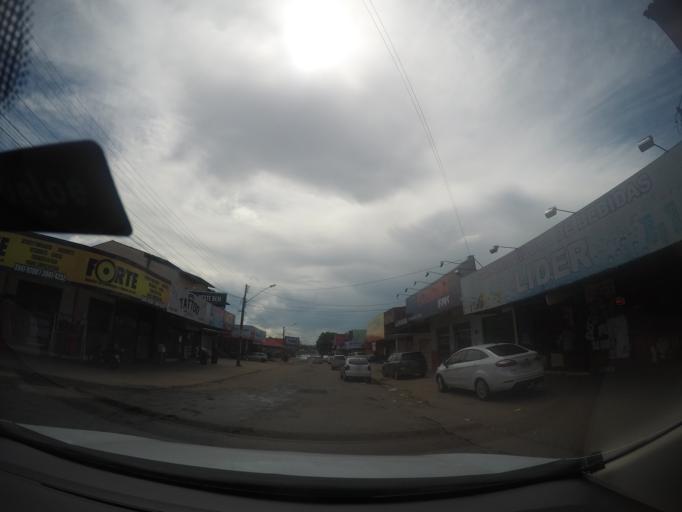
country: BR
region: Goias
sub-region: Goiania
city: Goiania
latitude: -16.6953
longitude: -49.3573
